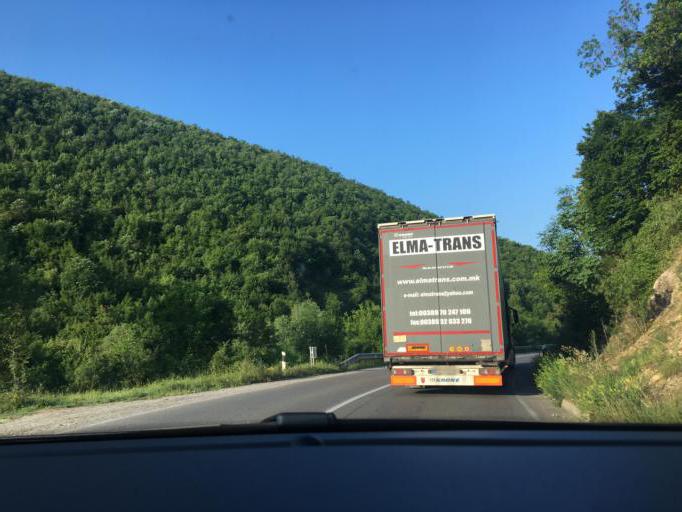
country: MK
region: Strumica
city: Strumica
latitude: 41.4010
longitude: 22.6158
